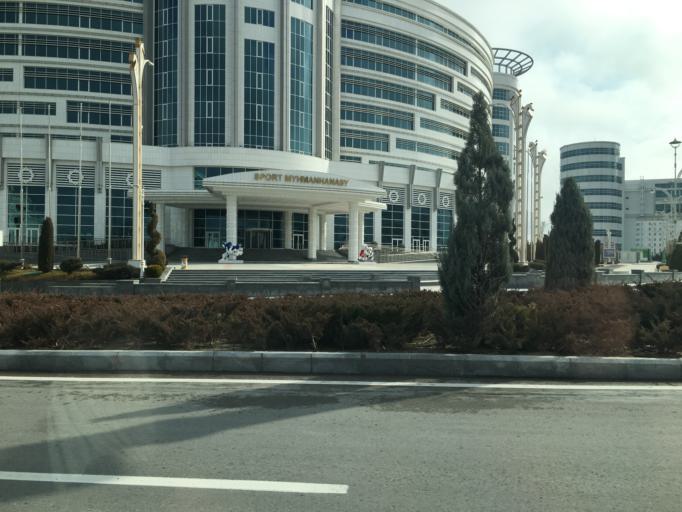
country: TM
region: Ahal
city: Ashgabat
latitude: 37.8973
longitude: 58.3703
